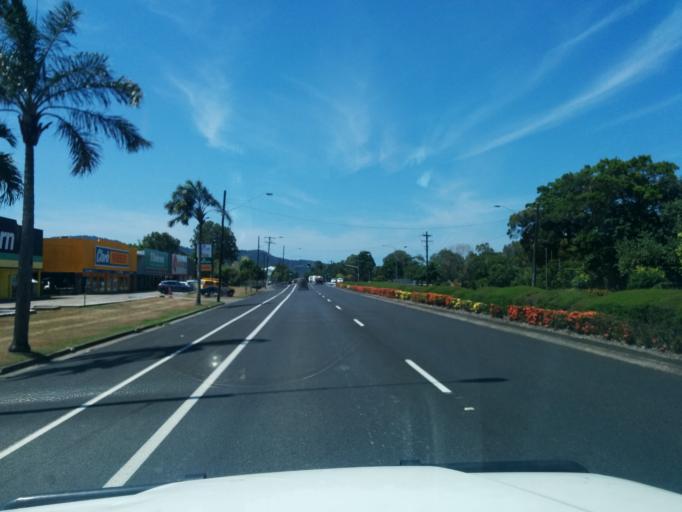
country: AU
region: Queensland
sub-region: Cairns
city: Woree
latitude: -16.9330
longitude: 145.7431
